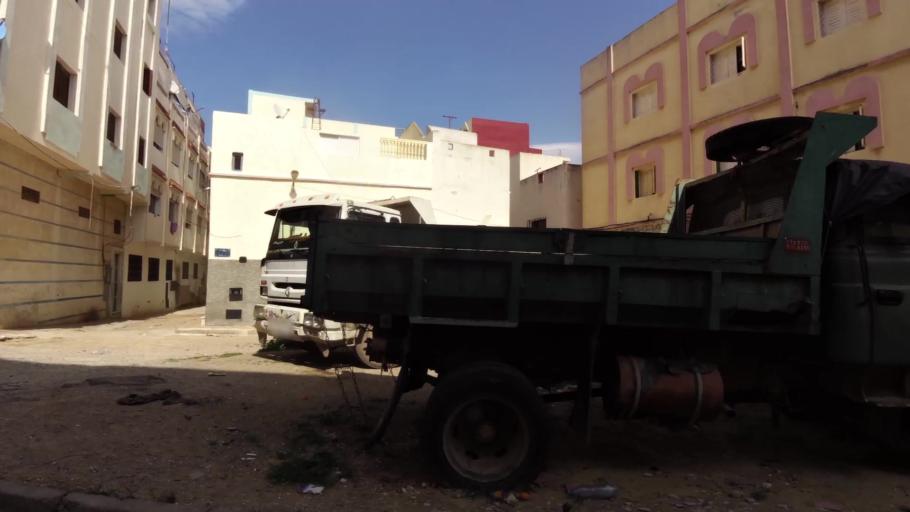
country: MA
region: Tanger-Tetouan
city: Tetouan
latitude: 35.5861
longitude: -5.3522
